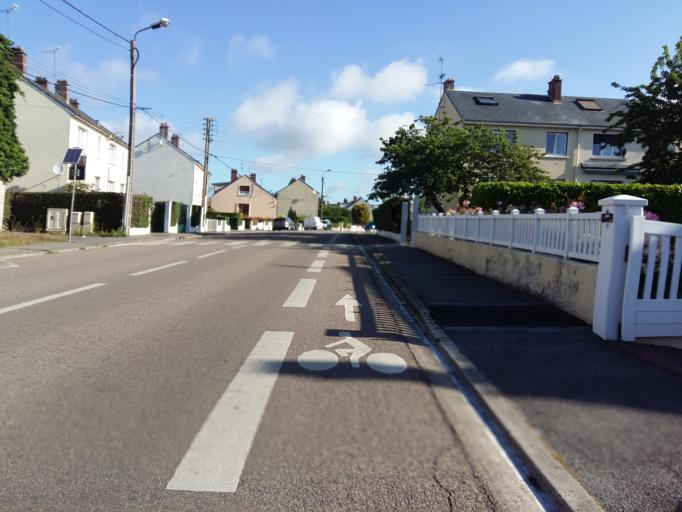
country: FR
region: Picardie
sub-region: Departement de la Somme
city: Rivery
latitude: 49.9069
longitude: 2.3265
